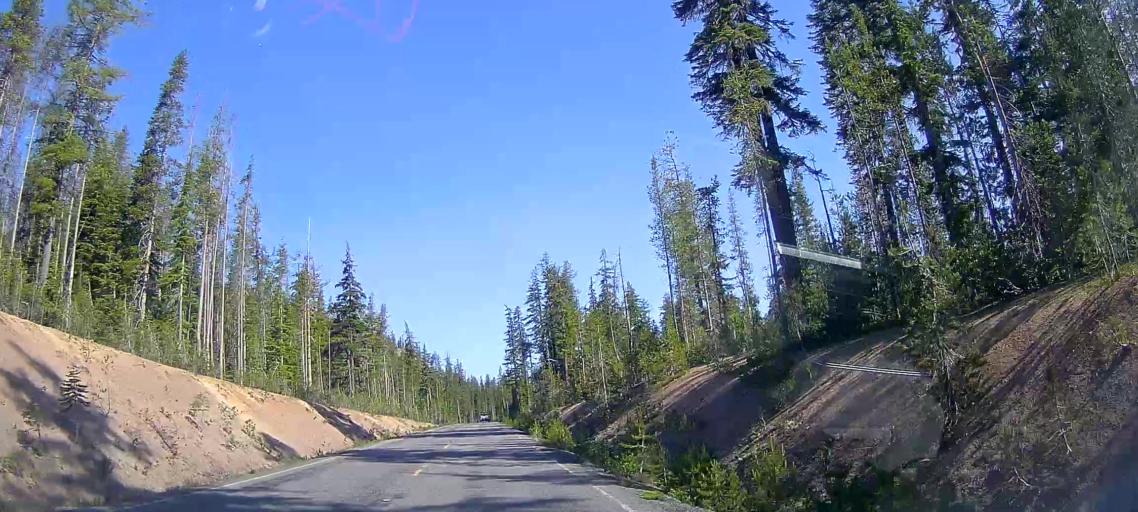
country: US
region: Oregon
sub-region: Jackson County
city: Shady Cove
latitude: 42.8506
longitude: -122.1491
